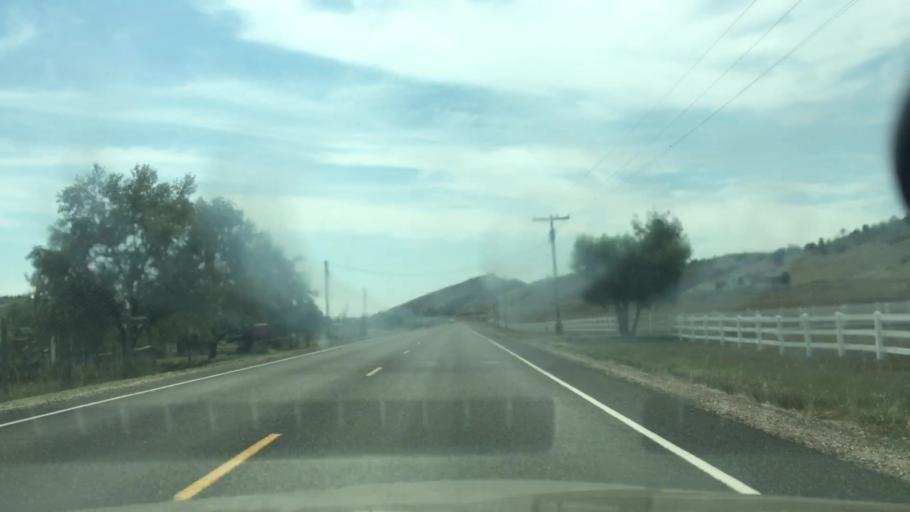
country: US
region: Colorado
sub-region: Larimer County
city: Campion
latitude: 40.3791
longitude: -105.1931
